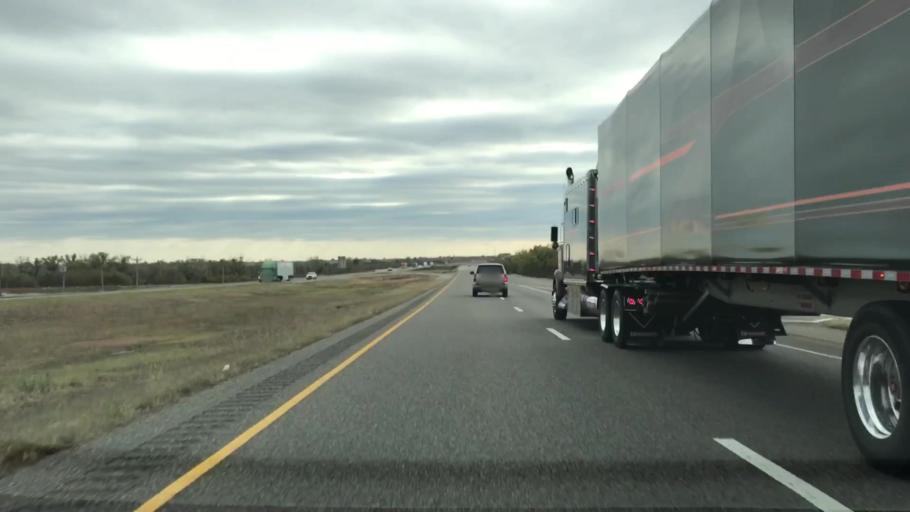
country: US
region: Oklahoma
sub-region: Beckham County
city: Sayre
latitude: 35.2900
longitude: -99.6208
